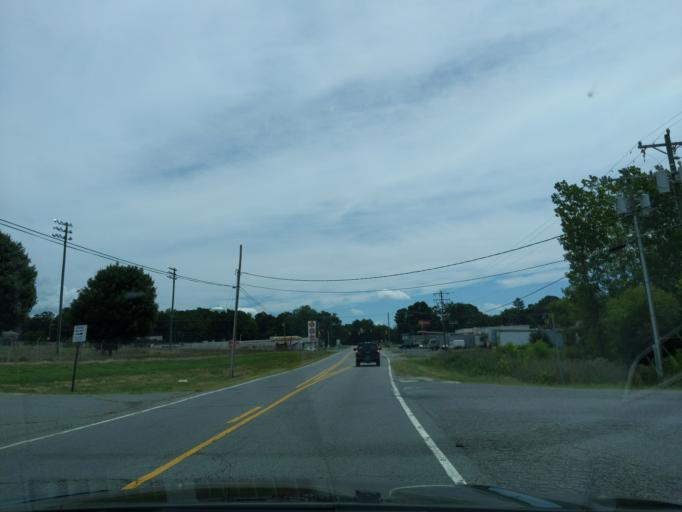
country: US
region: North Carolina
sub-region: Cabarrus County
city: Mount Pleasant
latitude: 35.4107
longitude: -80.4376
